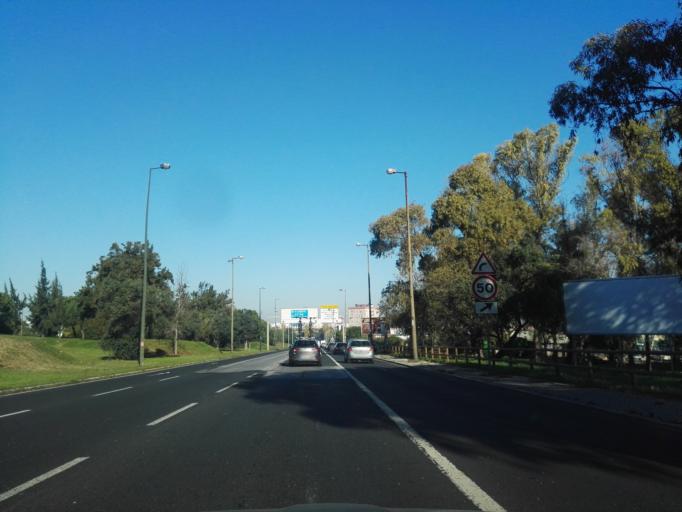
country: PT
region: Lisbon
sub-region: Loures
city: Moscavide
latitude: 38.7766
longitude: -9.1230
